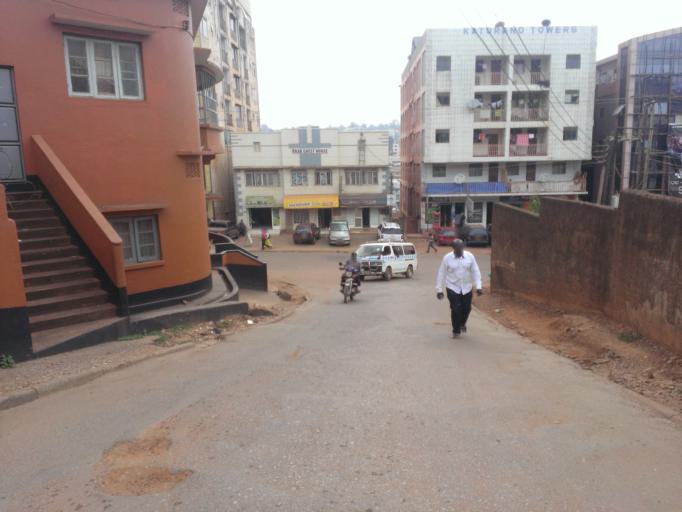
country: UG
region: Central Region
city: Kampala Central Division
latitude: 0.3162
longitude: 32.5700
